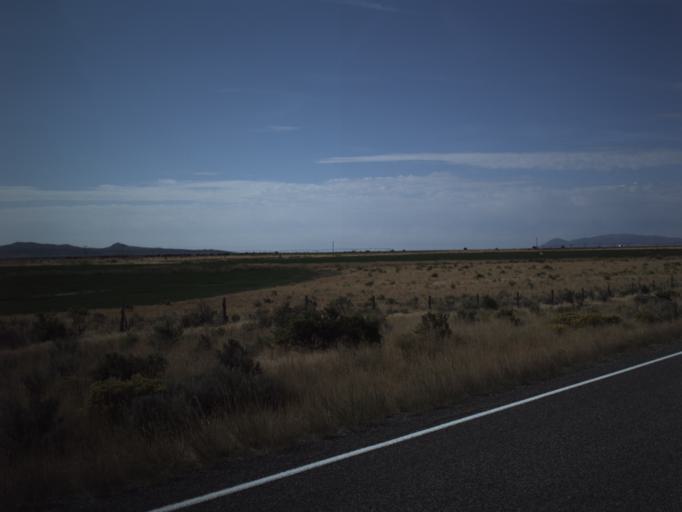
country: US
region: Idaho
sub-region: Cassia County
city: Burley
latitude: 41.7681
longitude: -113.5051
